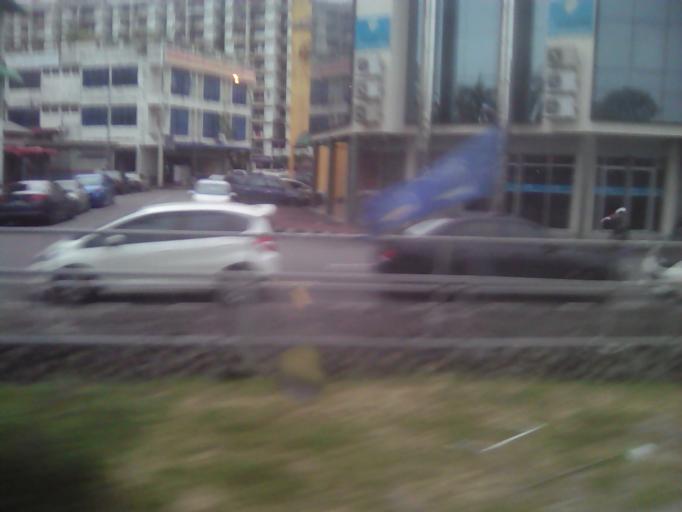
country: MY
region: Penang
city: Butterworth
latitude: 5.3991
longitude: 100.3731
